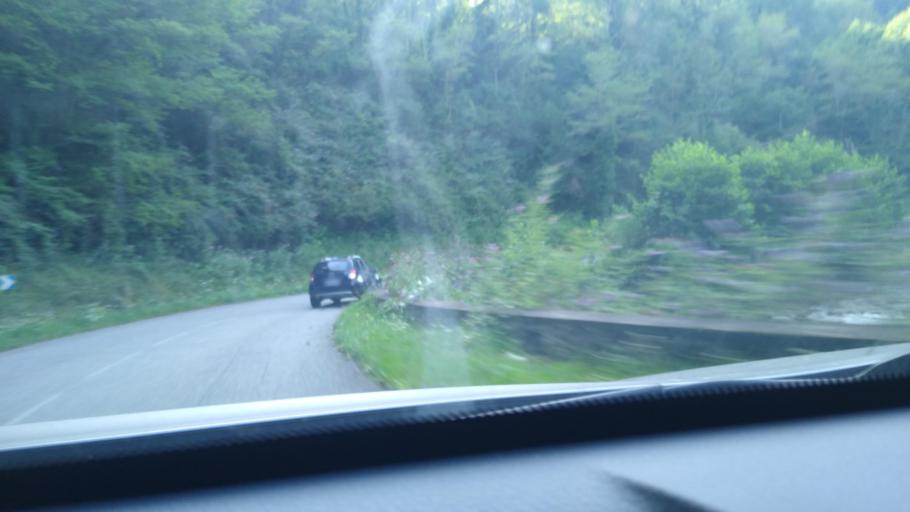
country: FR
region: Midi-Pyrenees
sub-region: Departement de l'Ariege
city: Saint-Girons
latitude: 42.8387
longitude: 1.1981
